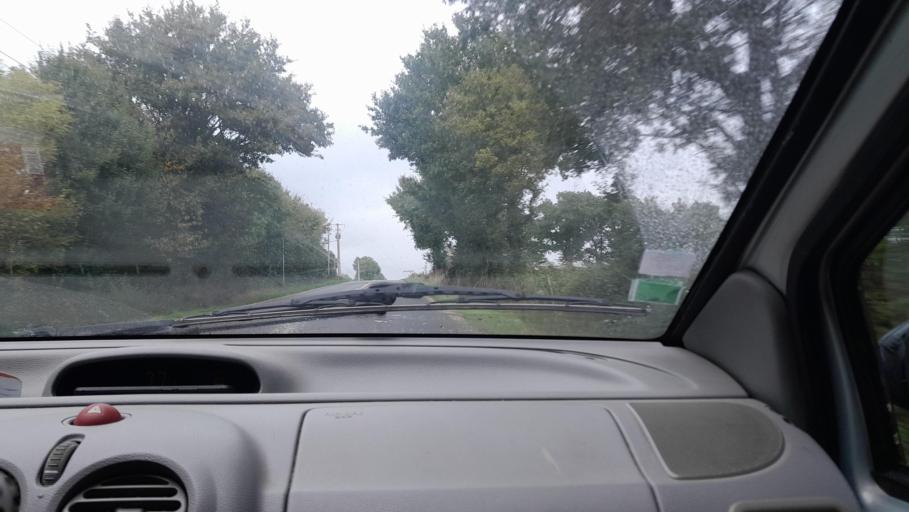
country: FR
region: Pays de la Loire
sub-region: Departement de la Mayenne
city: Congrier
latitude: 47.8232
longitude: -1.1444
